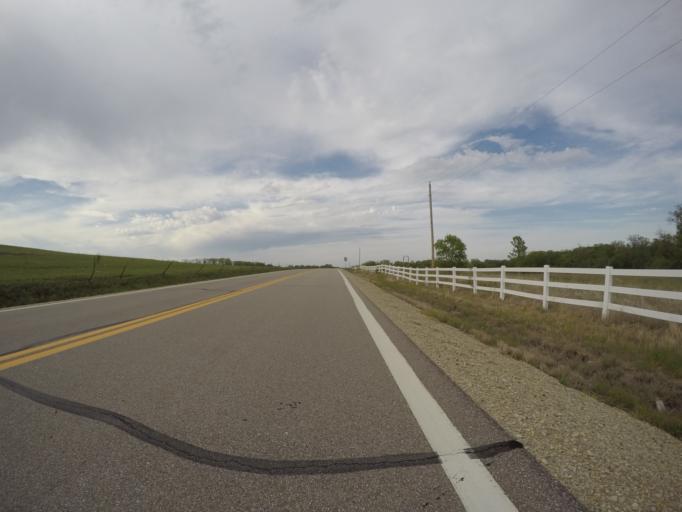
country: US
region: Kansas
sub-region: Riley County
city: Ogden
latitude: 39.0741
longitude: -96.6563
